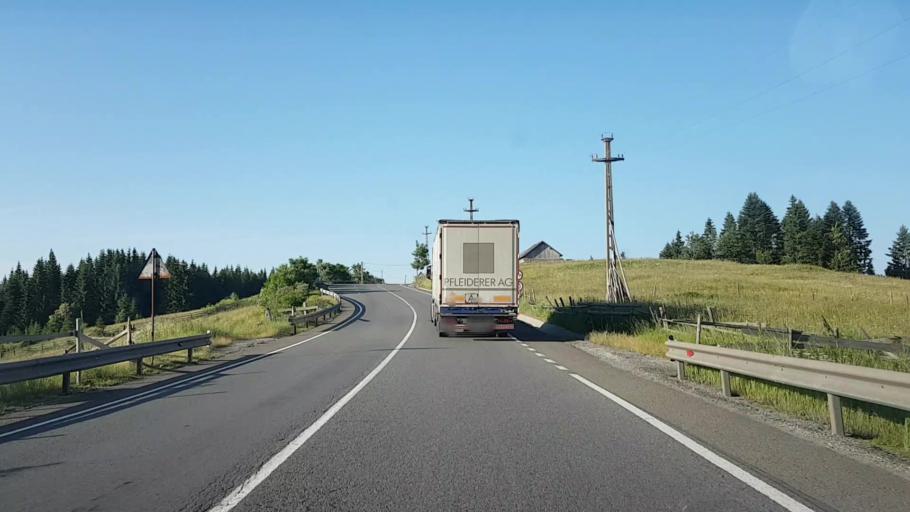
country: RO
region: Bistrita-Nasaud
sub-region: Comuna Lunca Ilvei
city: Lunca Ilvei
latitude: 47.2822
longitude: 25.0372
